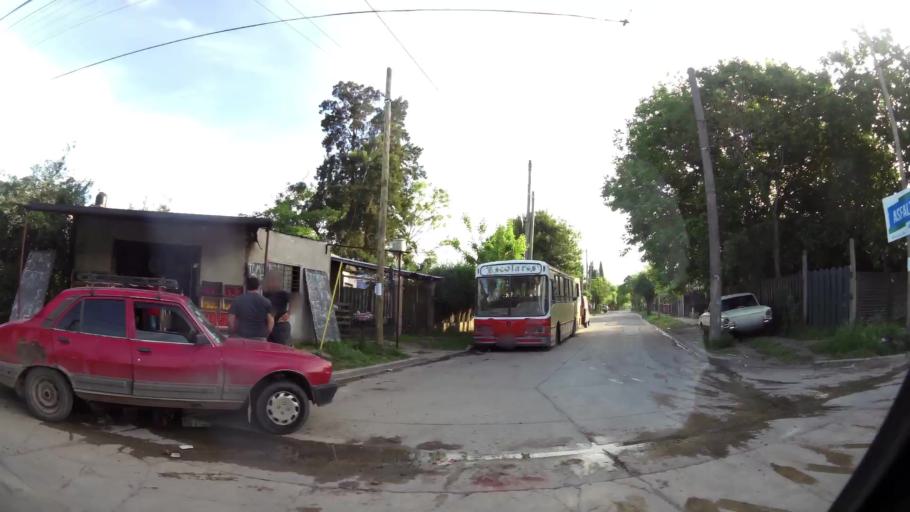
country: AR
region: Buenos Aires
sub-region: Partido de Almirante Brown
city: Adrogue
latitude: -34.7979
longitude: -58.3329
